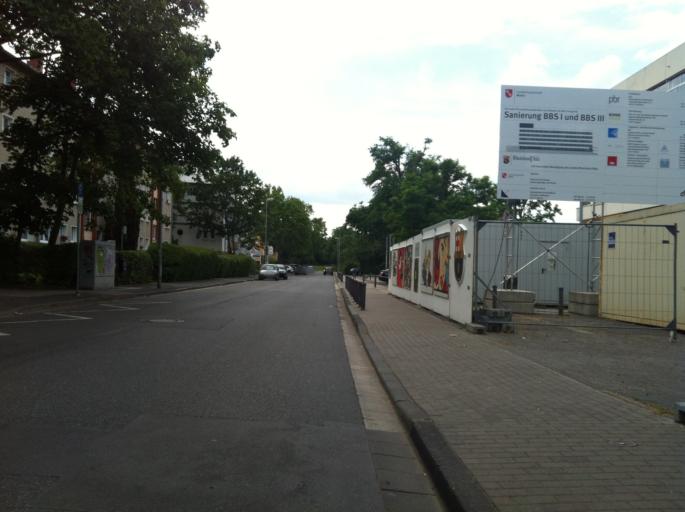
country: DE
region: Rheinland-Pfalz
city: Mainz
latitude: 50.0066
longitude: 8.2434
